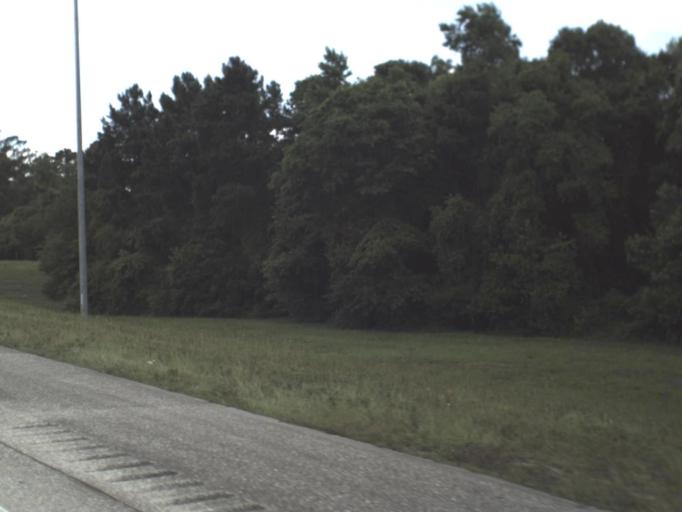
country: US
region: Florida
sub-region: Saint Johns County
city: Fruit Cove
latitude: 30.1682
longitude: -81.5380
